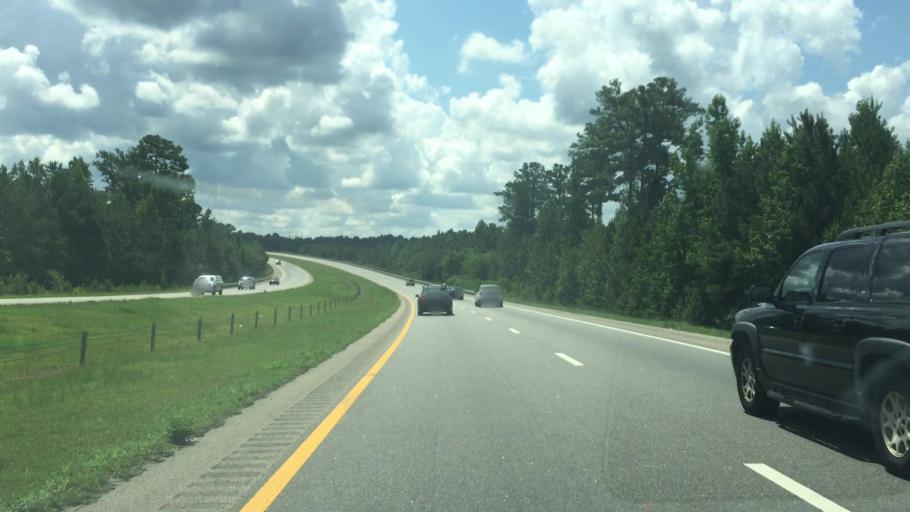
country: US
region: North Carolina
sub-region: Richmond County
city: East Rockingham
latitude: 34.8895
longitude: -79.7896
